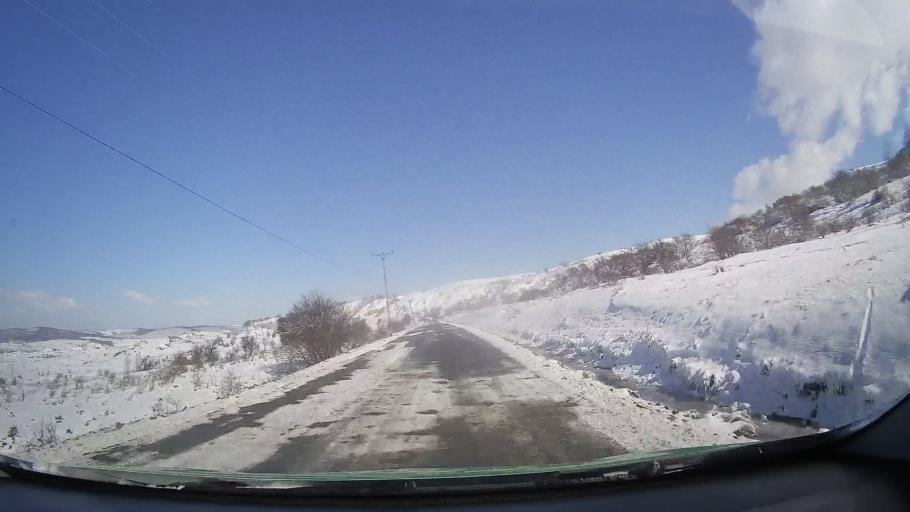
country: RO
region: Sibiu
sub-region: Comuna Avrig
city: Avrig
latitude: 45.7780
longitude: 24.3698
